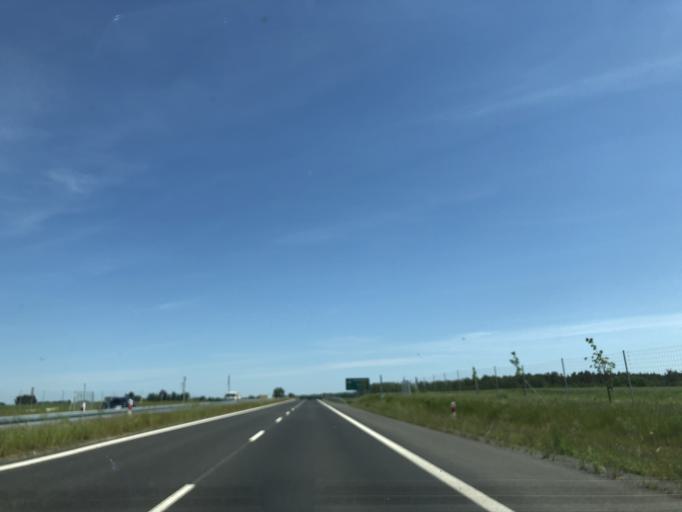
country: PL
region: West Pomeranian Voivodeship
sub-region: Powiat goleniowski
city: Osina
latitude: 53.6395
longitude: 15.0352
